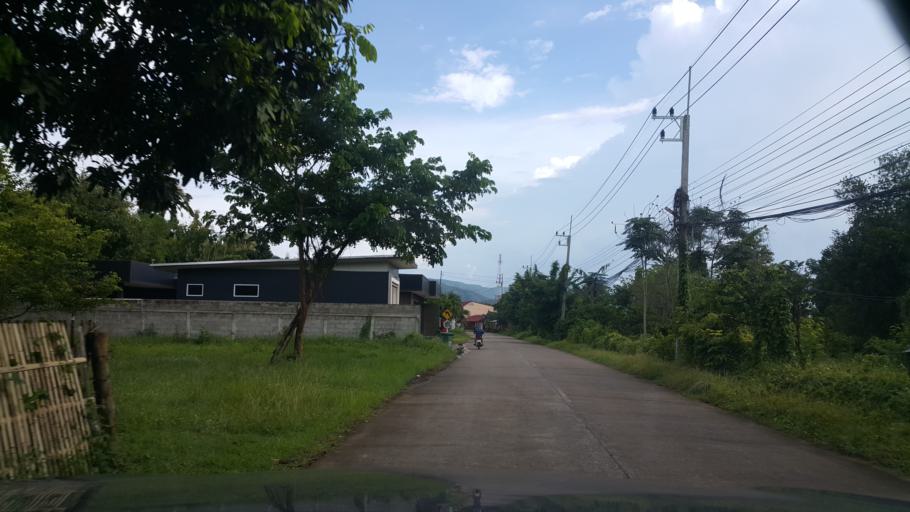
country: TH
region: Lampang
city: Thoen
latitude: 17.6196
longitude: 99.2269
